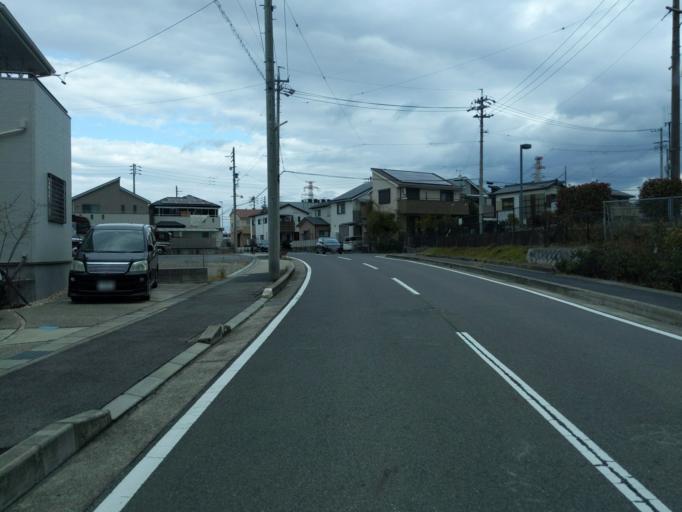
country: JP
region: Aichi
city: Kasugai
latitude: 35.2598
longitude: 136.9920
